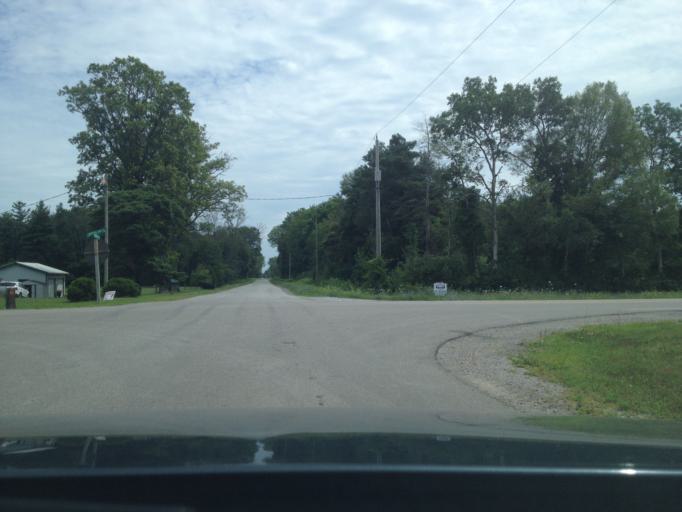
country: CA
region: Ontario
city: Norfolk County
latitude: 42.8548
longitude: -80.4026
